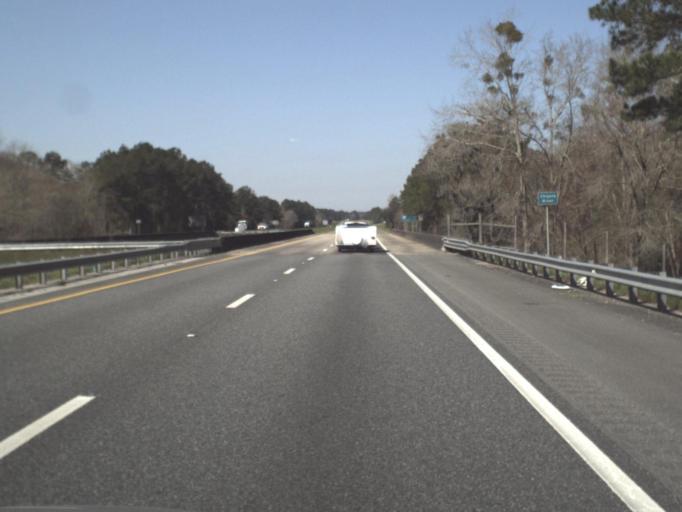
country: US
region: Florida
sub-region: Jackson County
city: Marianna
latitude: 30.7244
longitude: -85.1988
